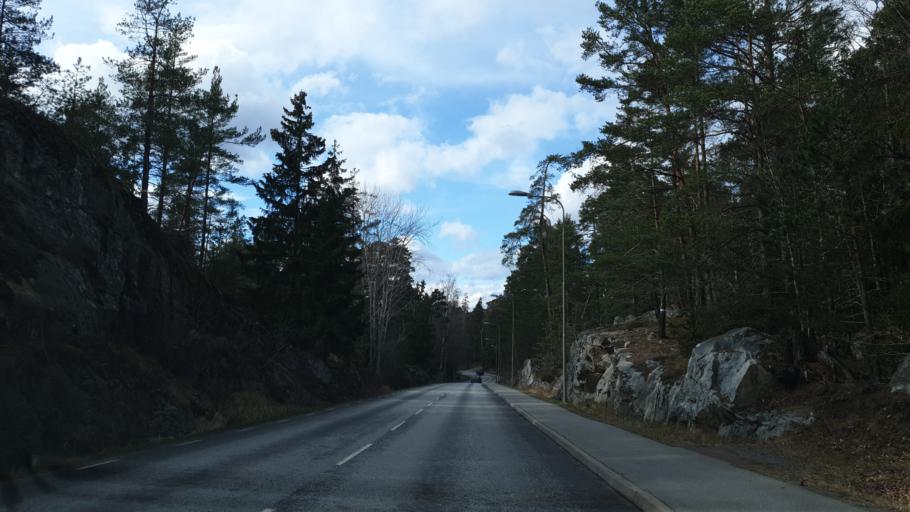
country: SE
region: Stockholm
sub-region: Nacka Kommun
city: Saltsjobaden
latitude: 59.2618
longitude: 18.3174
